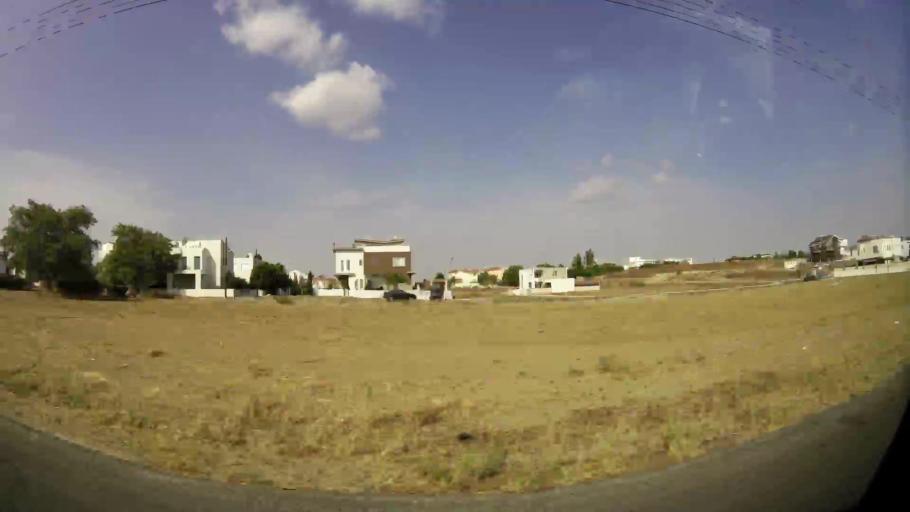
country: CY
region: Lefkosia
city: Geri
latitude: 35.0697
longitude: 33.3981
